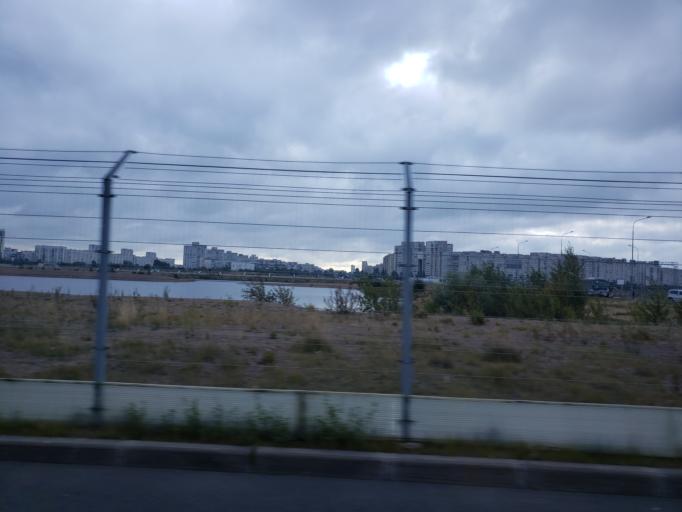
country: RU
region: St.-Petersburg
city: Vasyl'evsky Ostrov
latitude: 59.9486
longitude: 30.1959
